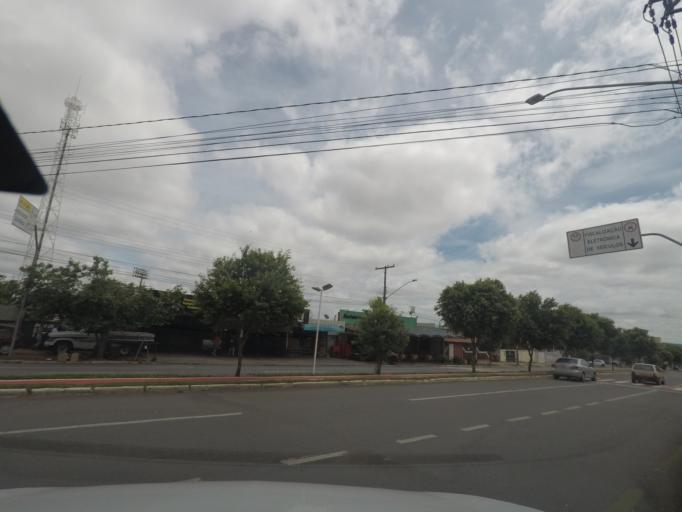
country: BR
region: Goias
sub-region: Goiania
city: Goiania
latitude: -16.6746
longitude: -49.2364
